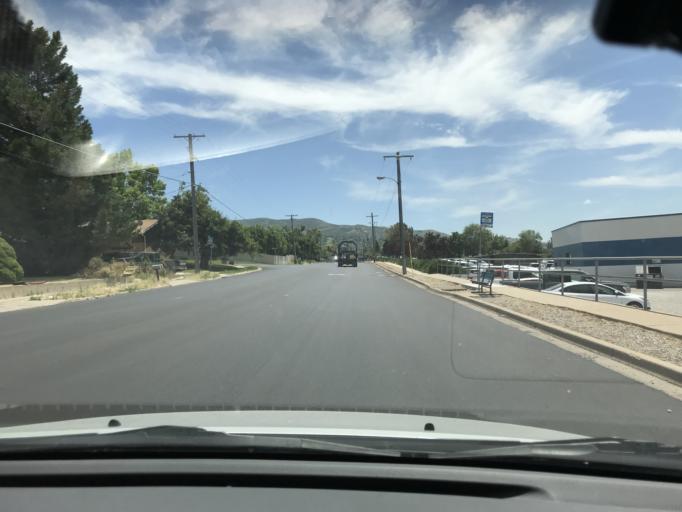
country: US
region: Utah
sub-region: Davis County
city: Woods Cross
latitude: 40.8649
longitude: -111.8923
